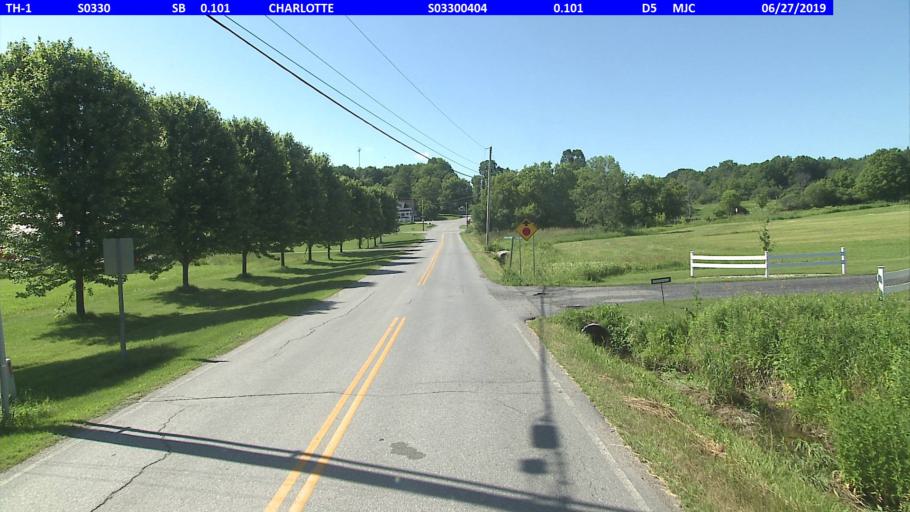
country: US
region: Vermont
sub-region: Chittenden County
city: Hinesburg
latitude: 44.3211
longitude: -73.1894
